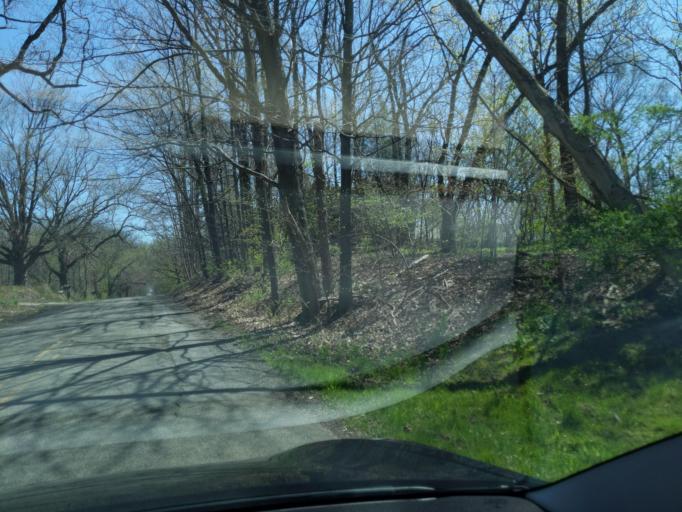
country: US
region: Michigan
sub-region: Eaton County
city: Eaton Rapids
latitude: 42.5530
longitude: -84.5968
